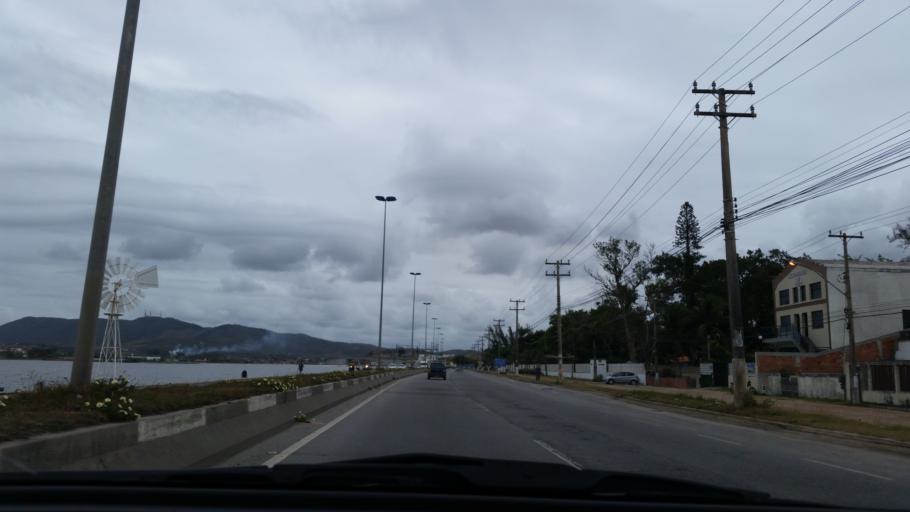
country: BR
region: Rio de Janeiro
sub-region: Sao Pedro Da Aldeia
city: Sao Pedro da Aldeia
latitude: -22.8309
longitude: -42.1075
